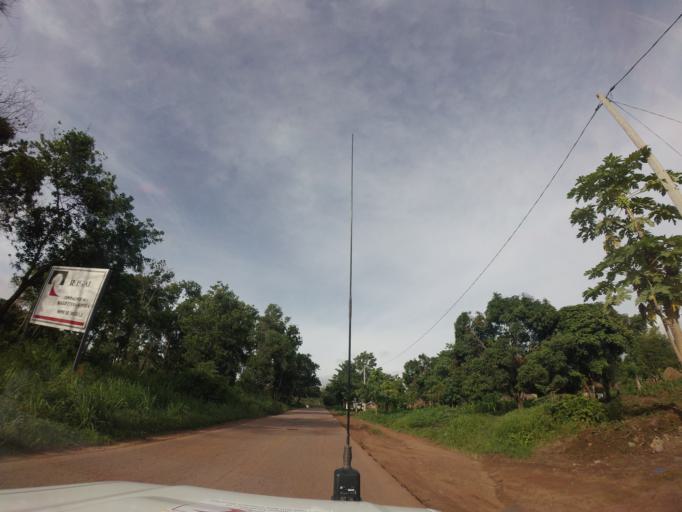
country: GN
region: Kindia
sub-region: Kindia
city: Kindia
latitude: 9.8576
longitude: -13.0829
